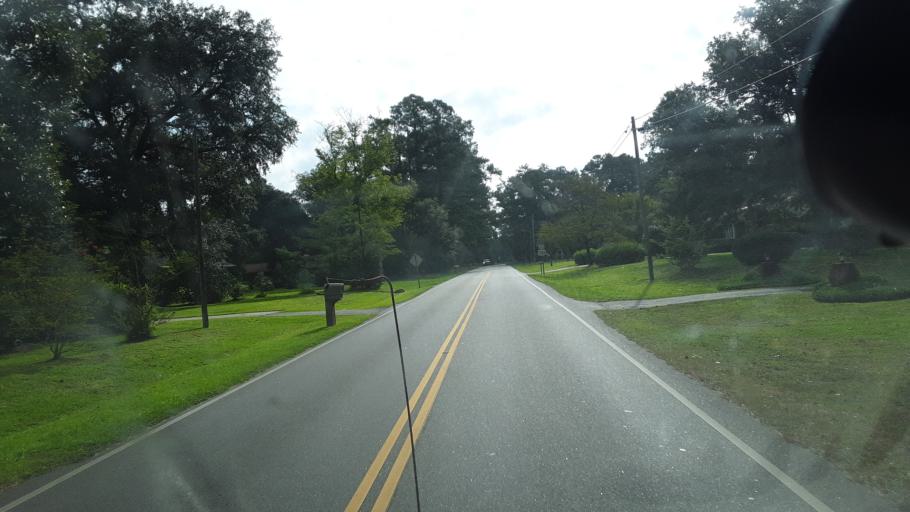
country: US
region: South Carolina
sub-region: Horry County
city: Conway
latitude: 33.8230
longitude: -79.0787
